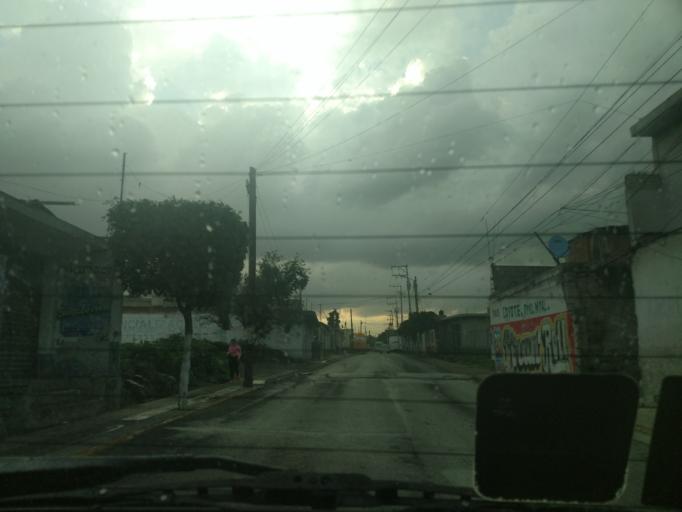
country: MX
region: Morelos
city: Coyotepec
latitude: 19.7726
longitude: -99.2037
